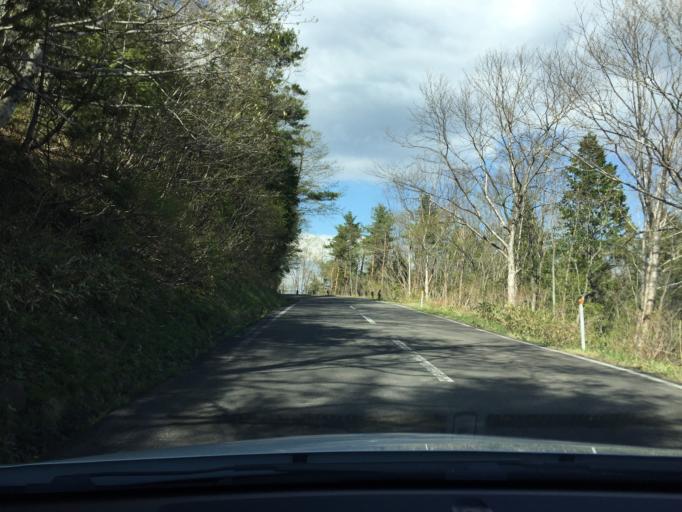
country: JP
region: Fukushima
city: Fukushima-shi
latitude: 37.7514
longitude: 140.2972
